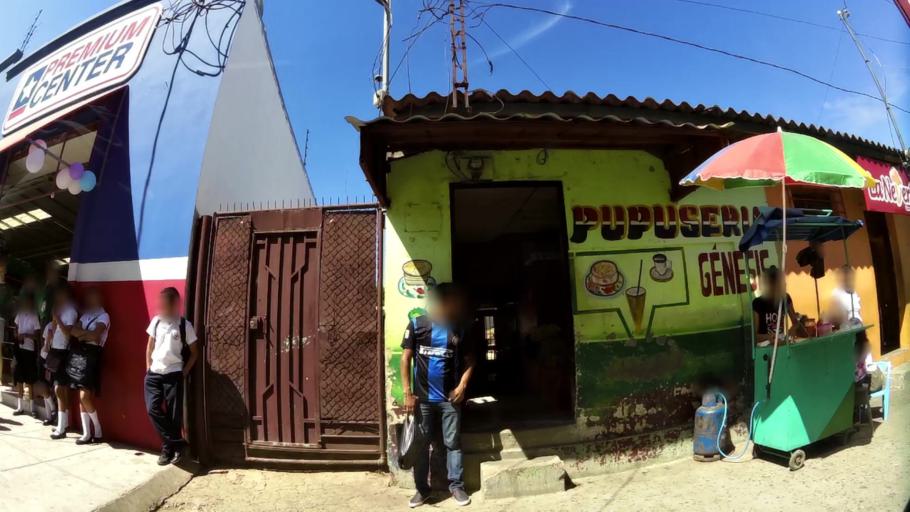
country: SV
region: Ahuachapan
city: Ahuachapan
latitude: 13.9242
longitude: -89.8466
